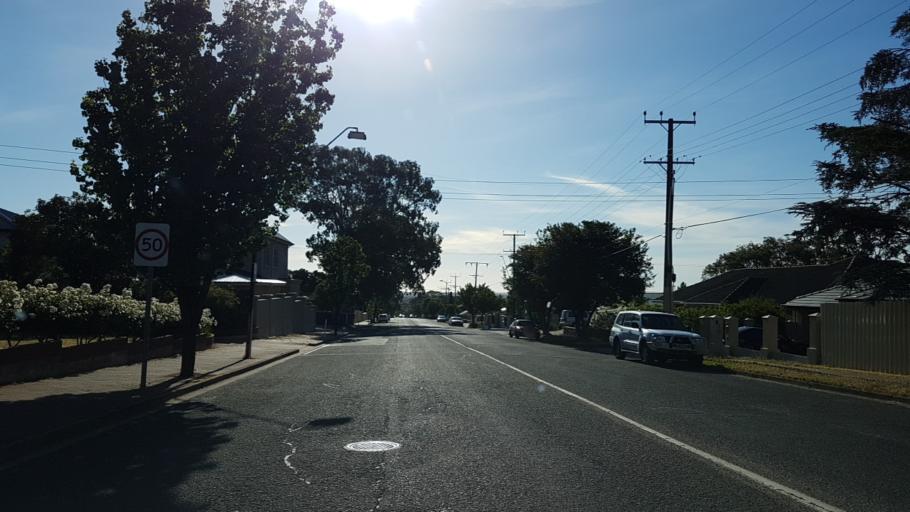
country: AU
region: South Australia
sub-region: Burnside
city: Wattle Park
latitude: -34.9023
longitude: 138.6837
